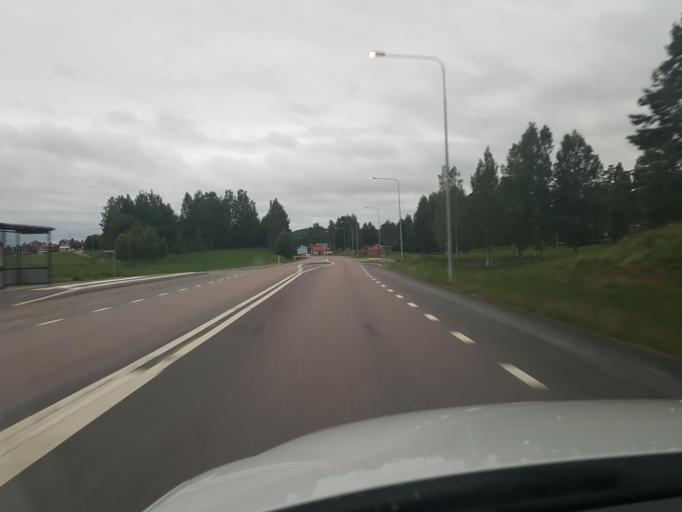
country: SE
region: Gaevleborg
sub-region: Bollnas Kommun
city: Bollnas
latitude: 61.3559
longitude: 16.4217
